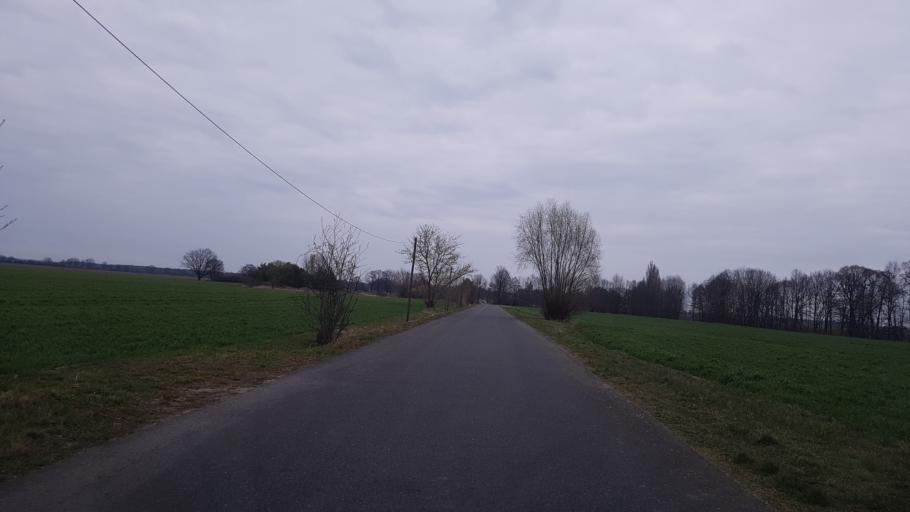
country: DE
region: Brandenburg
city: Sonnewalde
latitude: 51.6720
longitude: 13.6449
